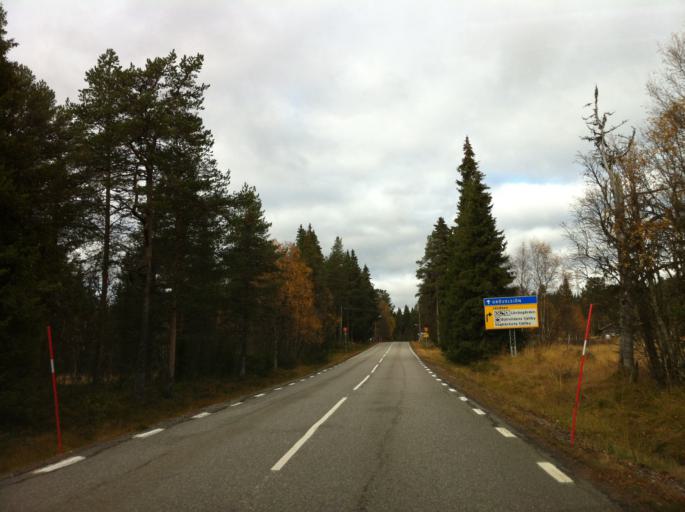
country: NO
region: Hedmark
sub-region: Engerdal
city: Engerdal
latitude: 62.0017
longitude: 12.4388
